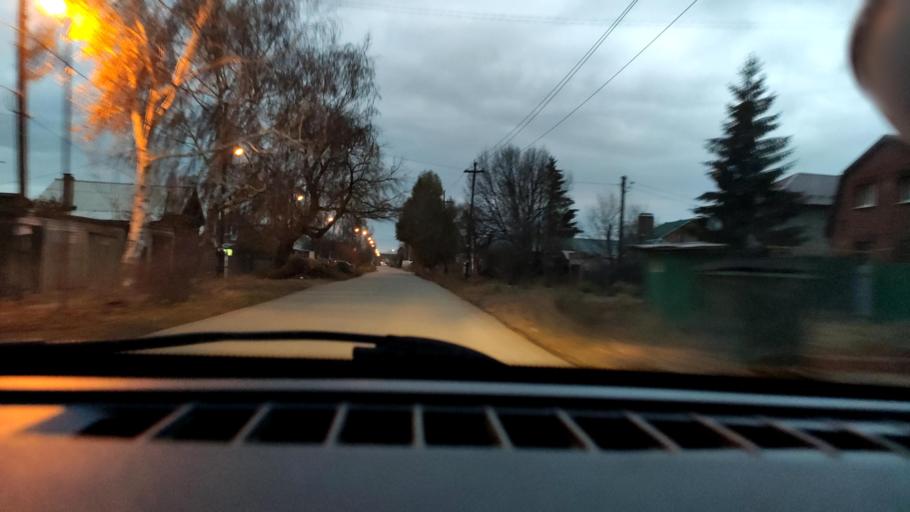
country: RU
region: Samara
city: Smyshlyayevka
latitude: 53.2450
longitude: 50.3278
